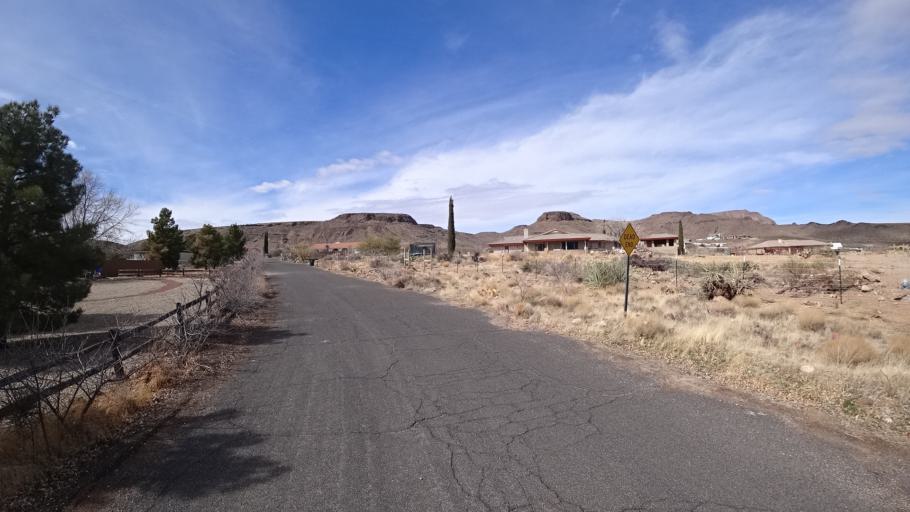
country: US
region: Arizona
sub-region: Mohave County
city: New Kingman-Butler
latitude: 35.2358
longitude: -114.0537
